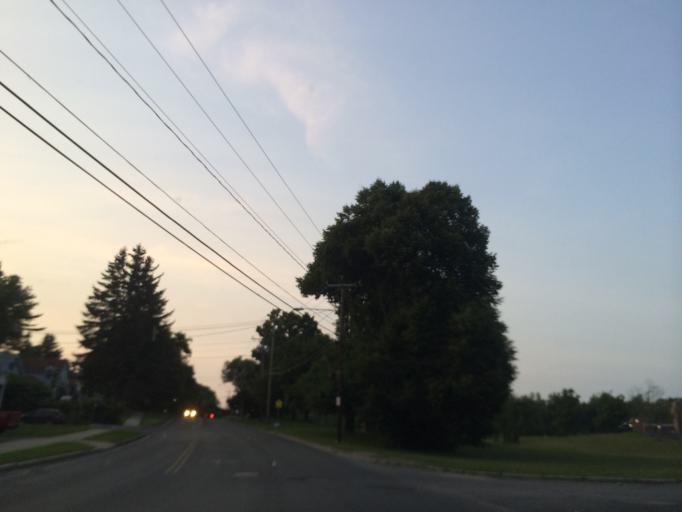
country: US
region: Massachusetts
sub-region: Berkshire County
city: Pittsfield
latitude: 42.4649
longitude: -73.2460
